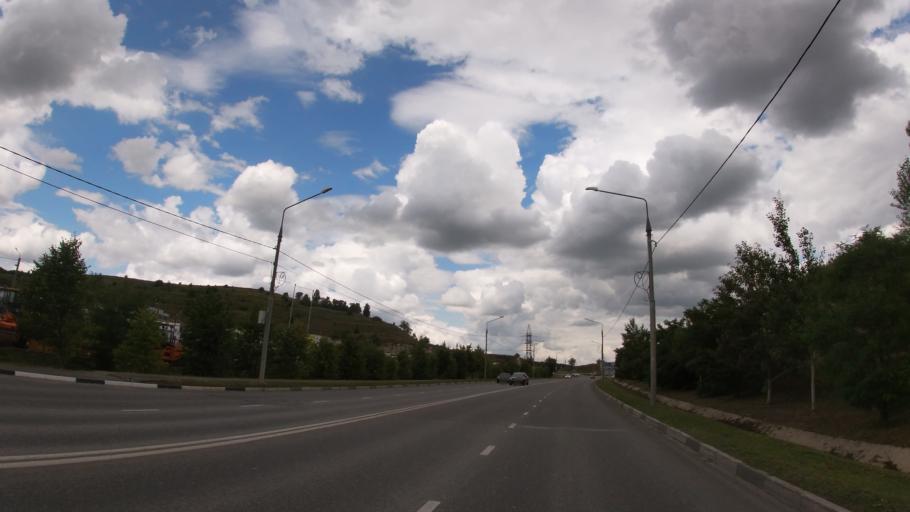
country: RU
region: Belgorod
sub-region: Belgorodskiy Rayon
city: Belgorod
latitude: 50.6152
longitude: 36.6141
